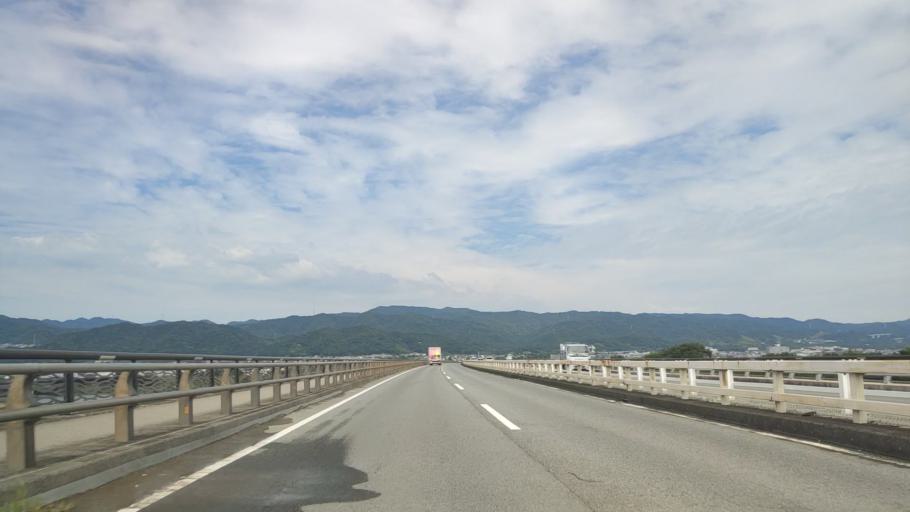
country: JP
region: Wakayama
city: Wakayama-shi
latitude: 34.2502
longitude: 135.2190
